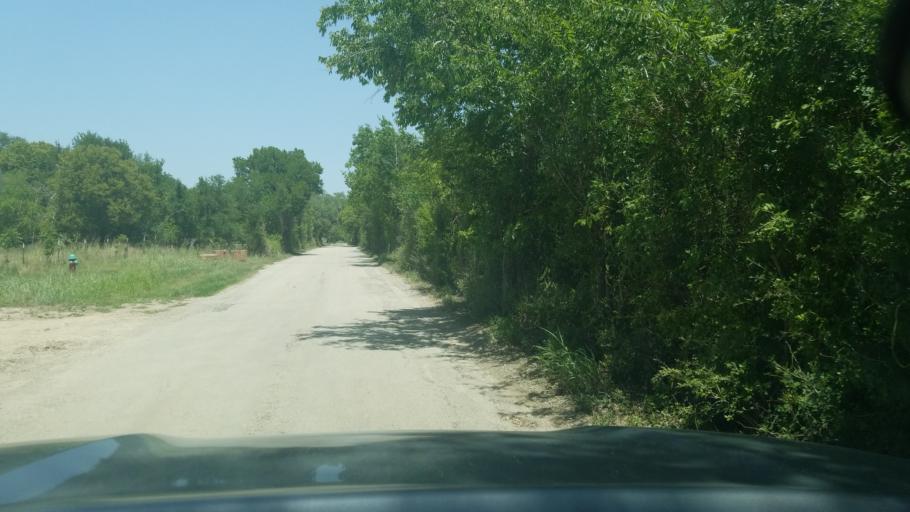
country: US
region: Texas
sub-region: Guadalupe County
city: Cibolo
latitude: 29.5908
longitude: -98.2287
